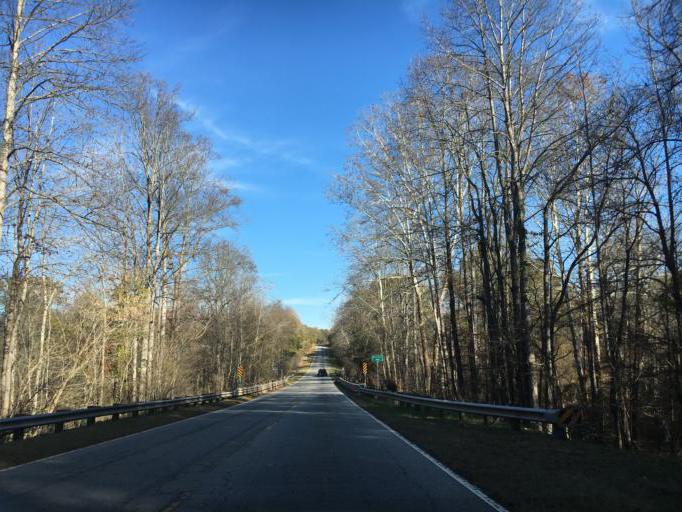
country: US
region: South Carolina
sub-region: Spartanburg County
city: Wellford
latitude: 34.9674
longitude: -82.1043
